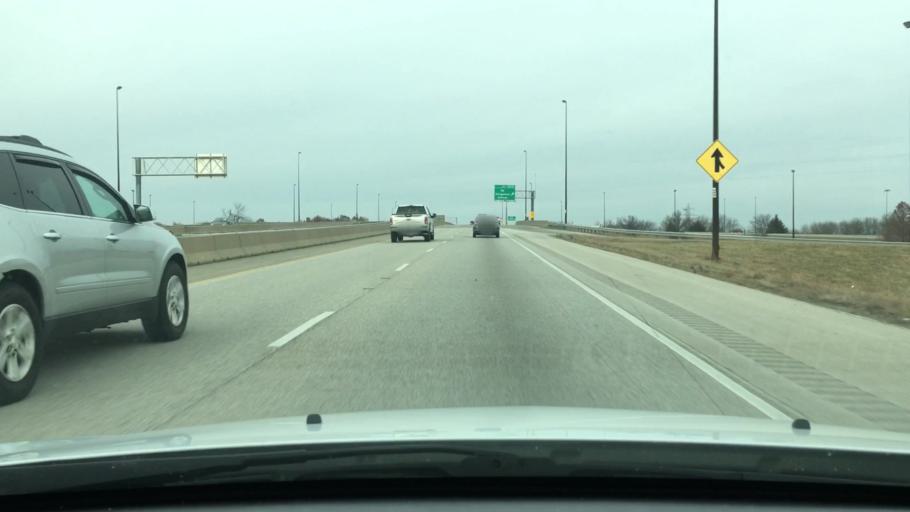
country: US
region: Illinois
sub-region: Sangamon County
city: Grandview
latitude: 39.8302
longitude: -89.5929
